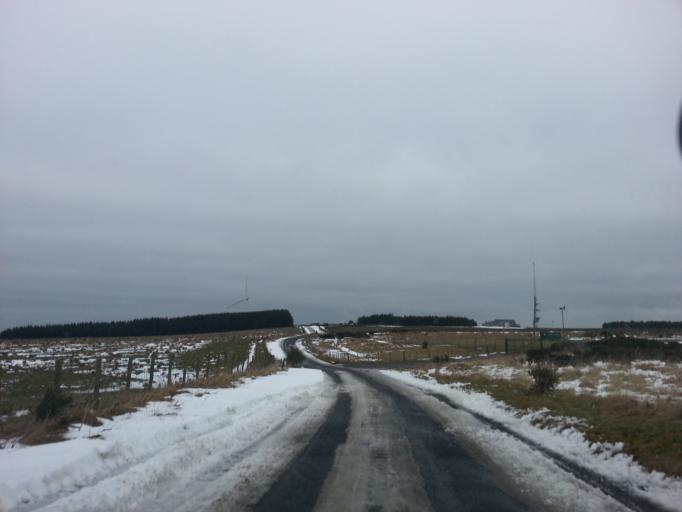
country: GB
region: England
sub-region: County Durham
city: Tow Law
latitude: 54.7591
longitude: -1.8148
